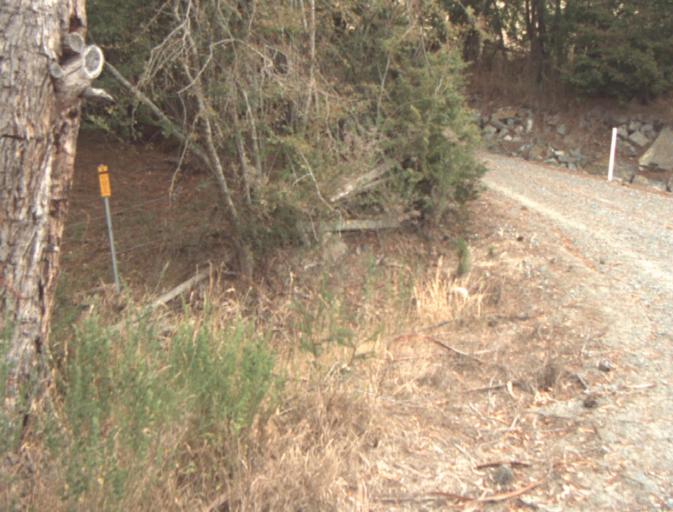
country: AU
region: Tasmania
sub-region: Launceston
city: Mayfield
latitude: -41.2482
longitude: 147.2013
